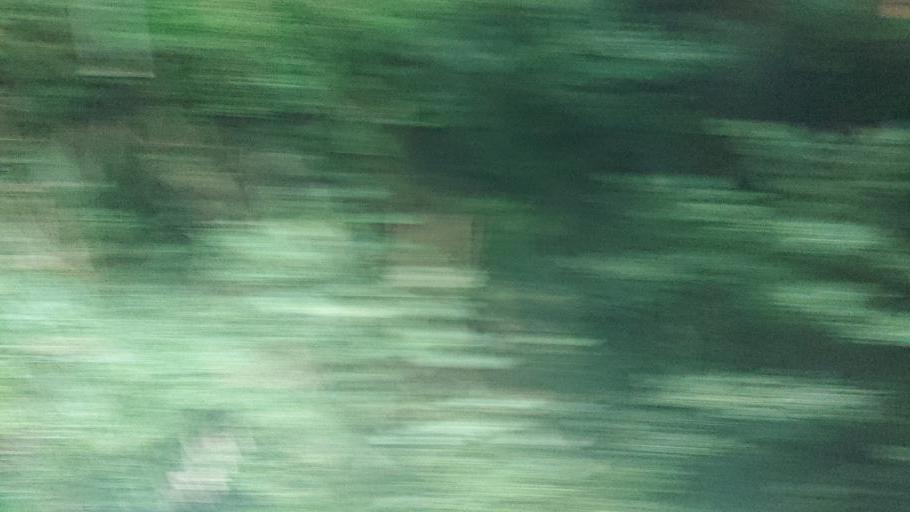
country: TW
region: Taiwan
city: Lugu
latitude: 23.5141
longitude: 120.7016
